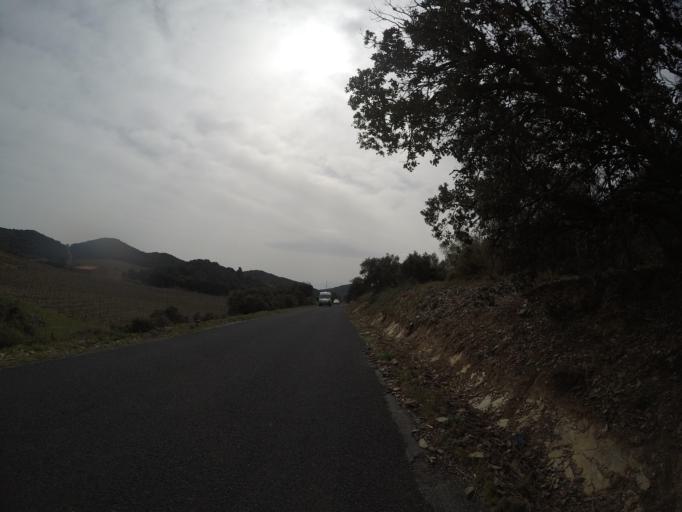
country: FR
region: Languedoc-Roussillon
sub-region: Departement des Pyrenees-Orientales
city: Corneilla-la-Riviere
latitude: 42.7392
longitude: 2.7297
